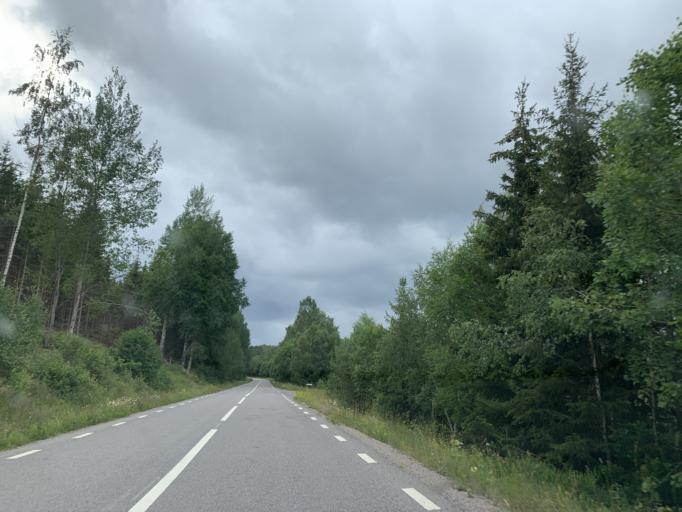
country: SE
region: Kalmar
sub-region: Vasterviks Kommun
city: Overum
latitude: 58.0189
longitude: 16.1482
